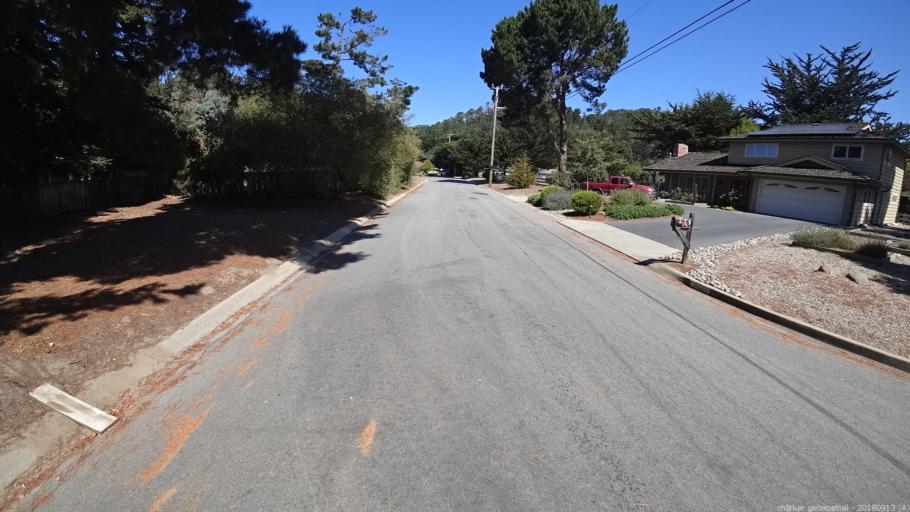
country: US
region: California
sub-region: Monterey County
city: Carmel-by-the-Sea
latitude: 36.5381
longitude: -121.8683
